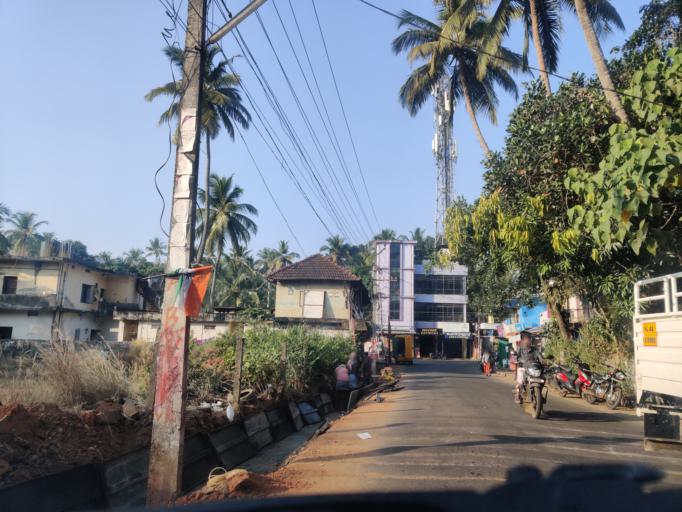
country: IN
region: Kerala
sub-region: Malappuram
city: Ponnani
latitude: 10.7333
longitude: 76.0128
